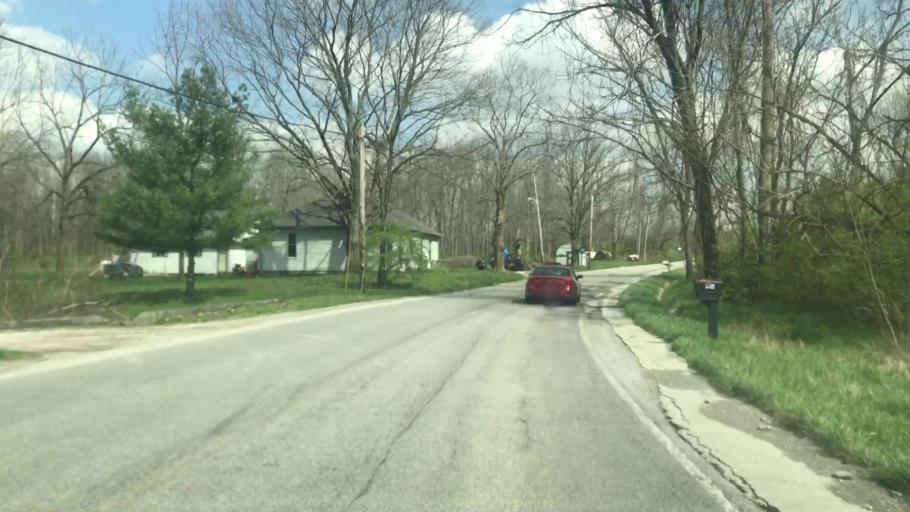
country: US
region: Indiana
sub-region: Johnson County
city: Waterloo
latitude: 39.5518
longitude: -86.2106
